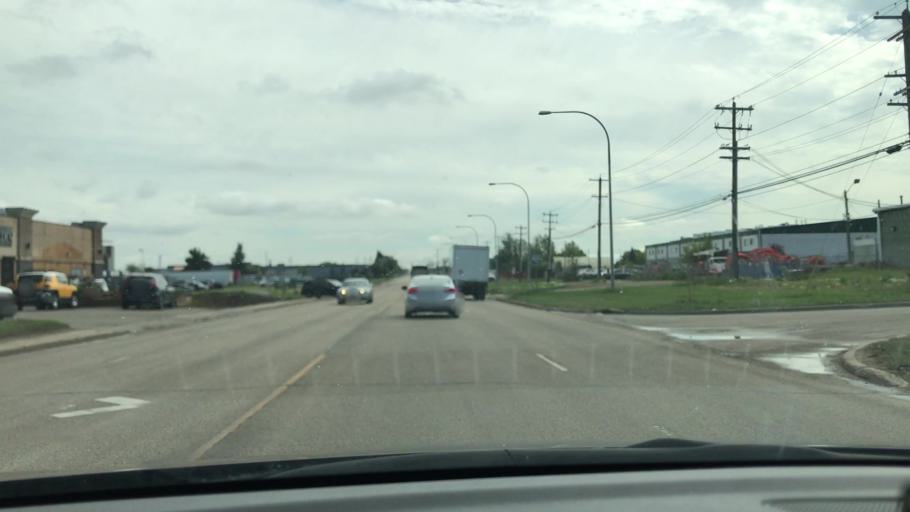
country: CA
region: Alberta
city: Edmonton
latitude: 53.5125
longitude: -113.4168
